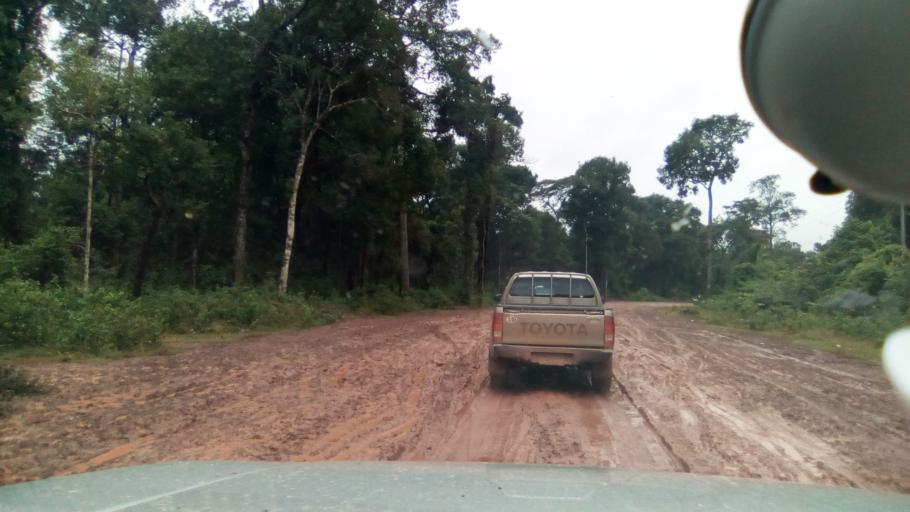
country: LA
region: Attapu
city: Attapu
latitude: 14.6837
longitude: 106.5533
